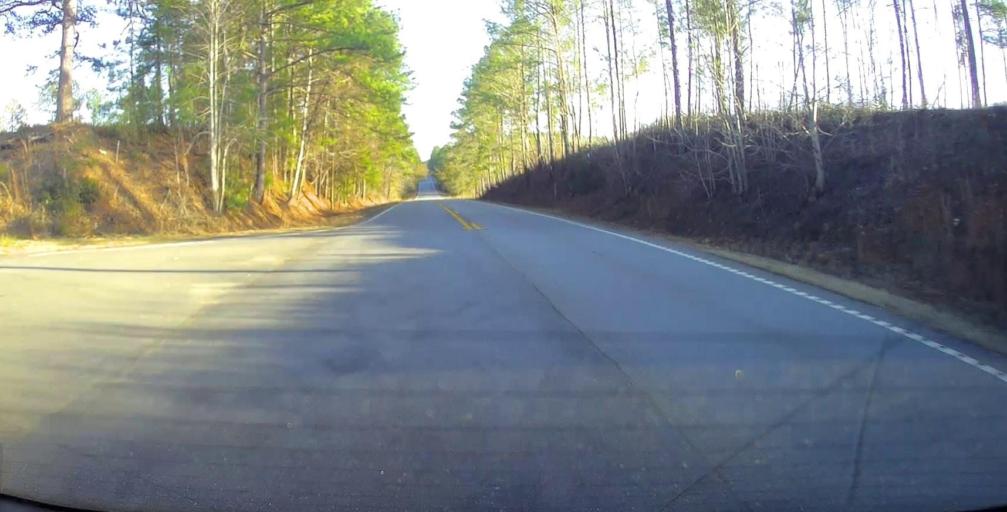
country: US
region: Alabama
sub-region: Chambers County
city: Valley
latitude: 32.8325
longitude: -85.1121
